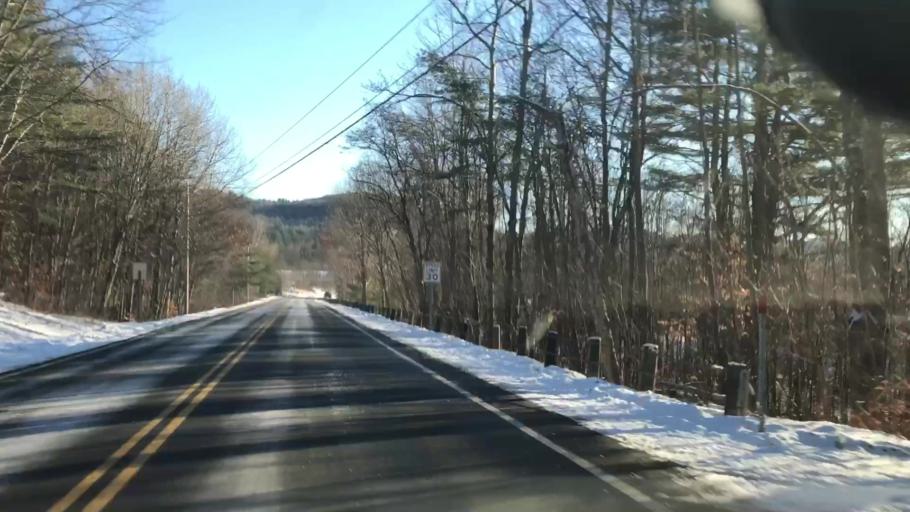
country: US
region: New Hampshire
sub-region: Grafton County
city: Haverhill
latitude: 43.9741
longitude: -72.0799
